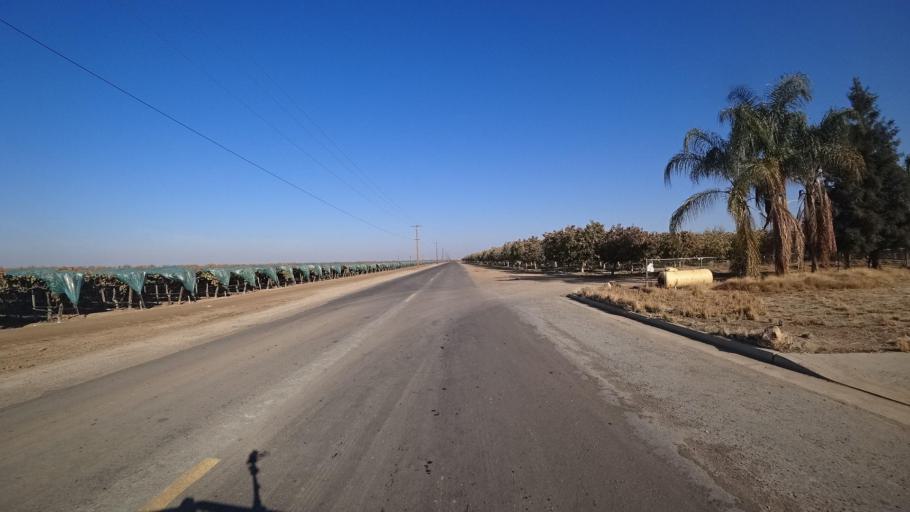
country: US
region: California
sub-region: Tulare County
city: Richgrove
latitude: 35.7538
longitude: -119.1341
